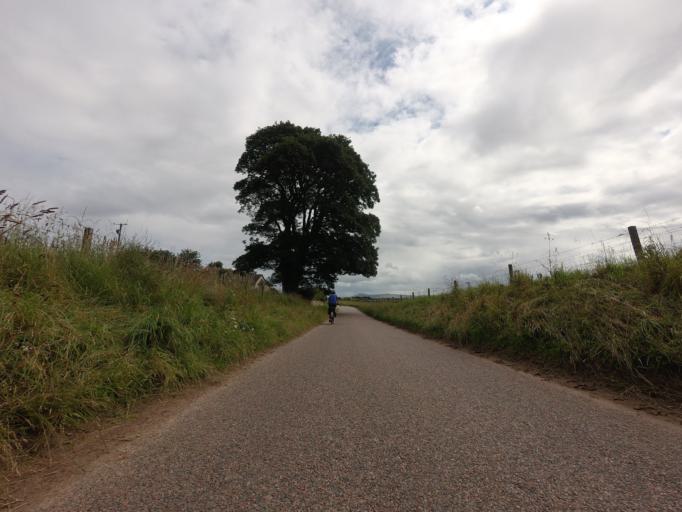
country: GB
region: Scotland
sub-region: Moray
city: Fochabers
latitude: 57.6669
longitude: -3.1432
